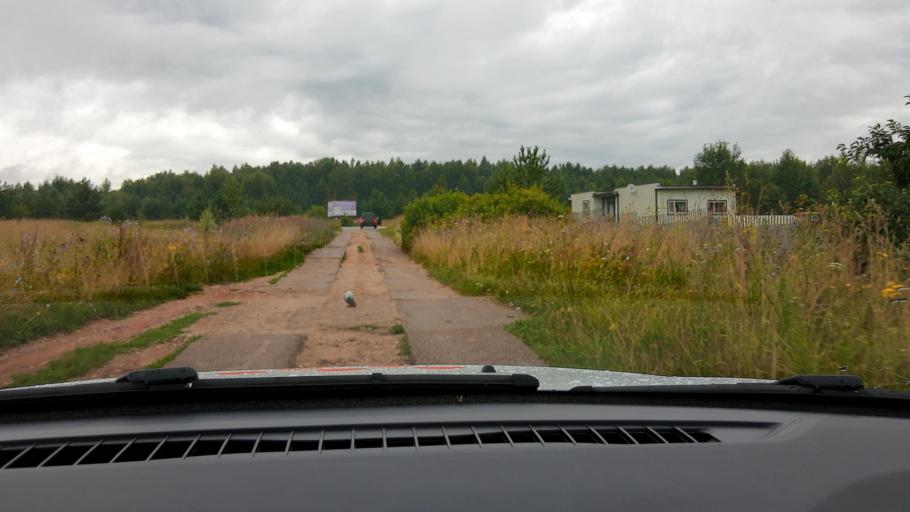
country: RU
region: Nizjnij Novgorod
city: Surovatikha
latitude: 55.9437
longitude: 43.9160
